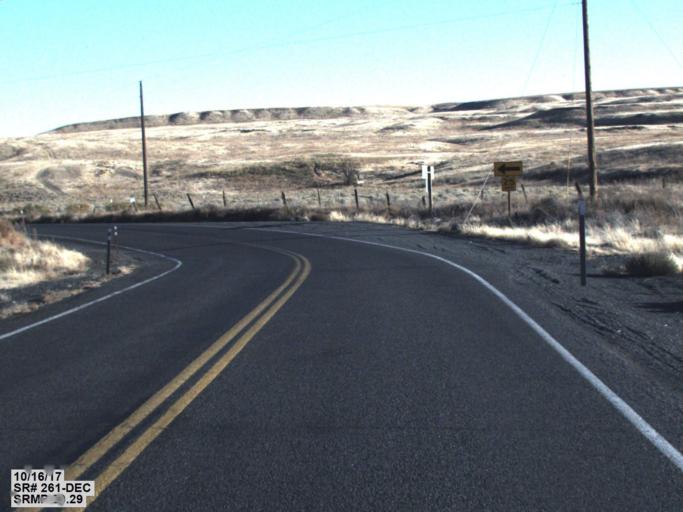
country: US
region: Washington
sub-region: Adams County
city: Ritzville
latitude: 46.7000
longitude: -118.4113
